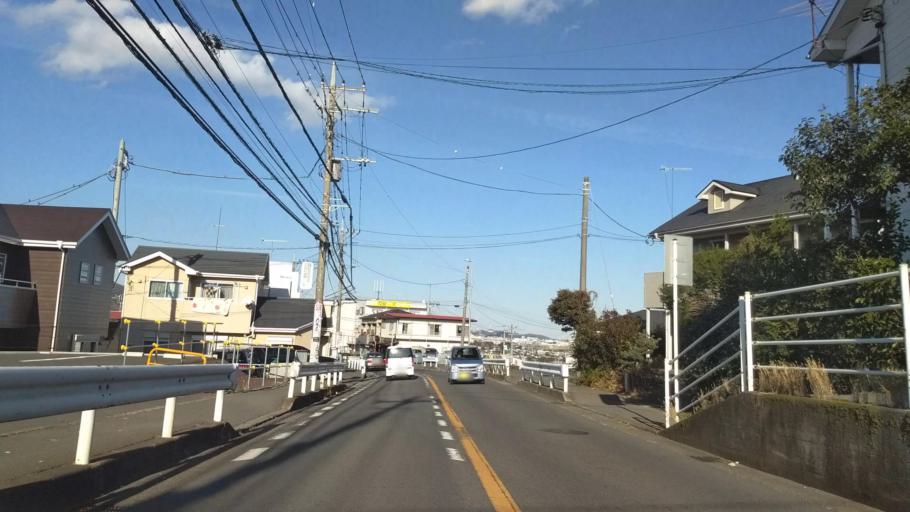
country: JP
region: Kanagawa
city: Isehara
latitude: 35.3678
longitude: 139.2736
